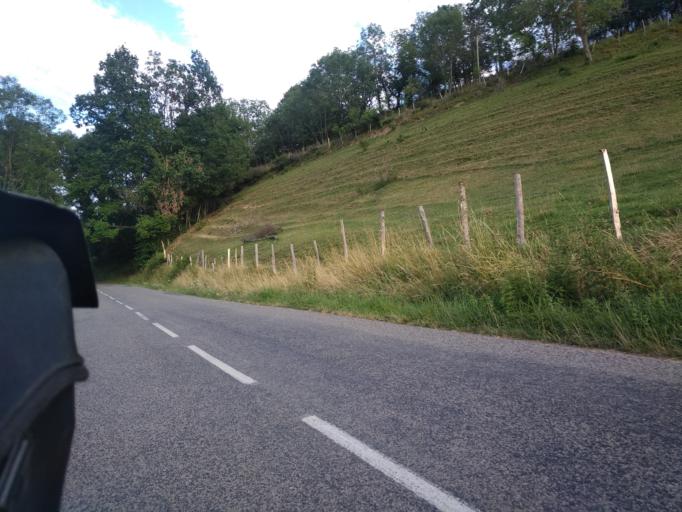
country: FR
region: Rhone-Alpes
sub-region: Departement du Rhone
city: Montrottier
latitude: 45.7866
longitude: 4.4930
